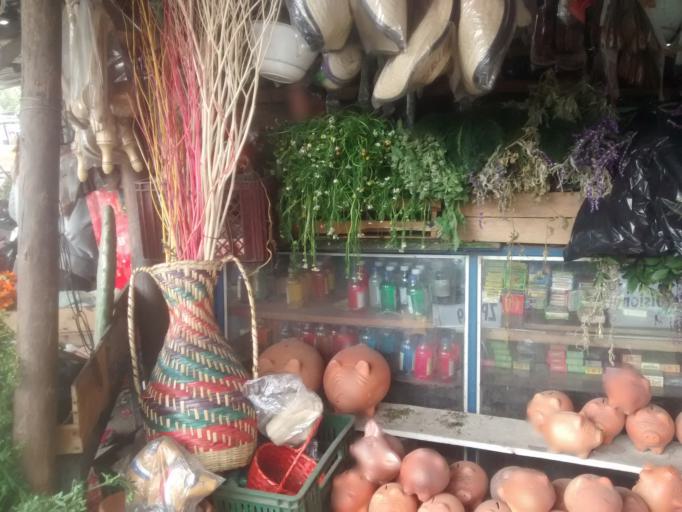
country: CO
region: Cundinamarca
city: Cota
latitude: 4.7446
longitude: -74.1065
